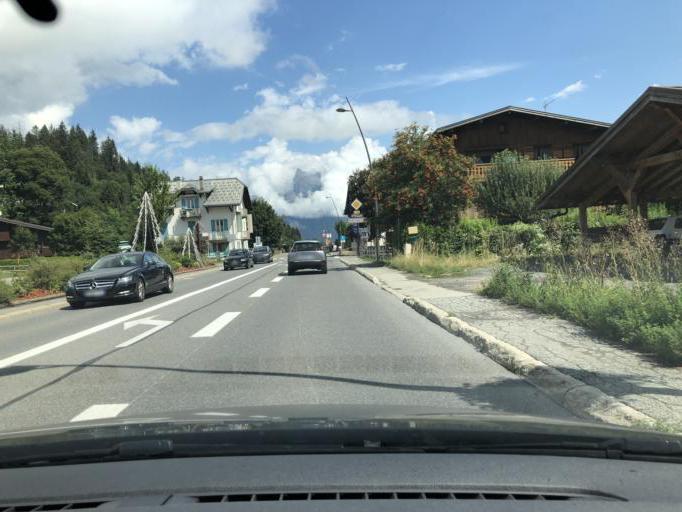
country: FR
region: Rhone-Alpes
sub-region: Departement de la Haute-Savoie
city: Megeve
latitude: 45.8683
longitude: 6.6281
